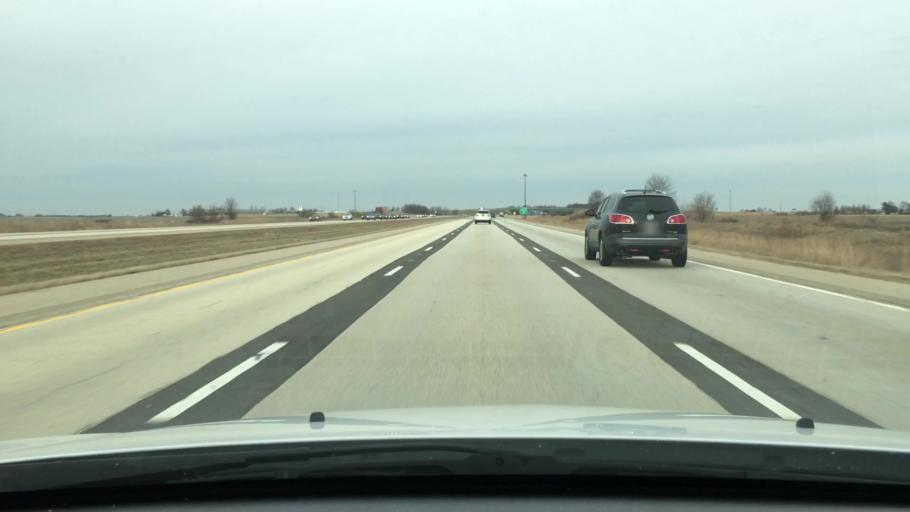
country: US
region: Illinois
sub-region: Sangamon County
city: Williamsville
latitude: 40.0113
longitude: -89.4996
